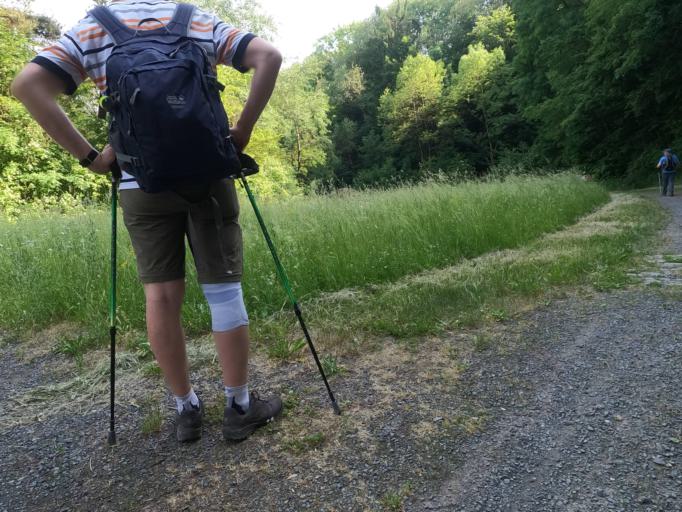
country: DE
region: Rheinland-Pfalz
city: Hahn bei Marienberg
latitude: 50.6470
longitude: 7.9353
